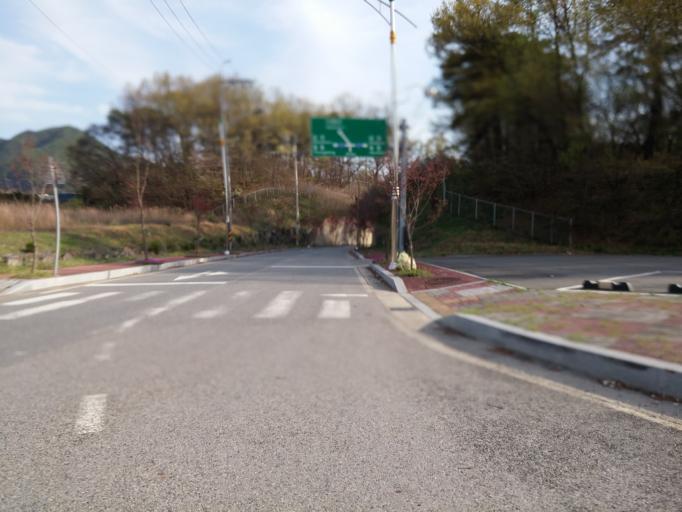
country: KR
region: Chungcheongbuk-do
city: Okcheon
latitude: 36.2736
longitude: 127.5890
